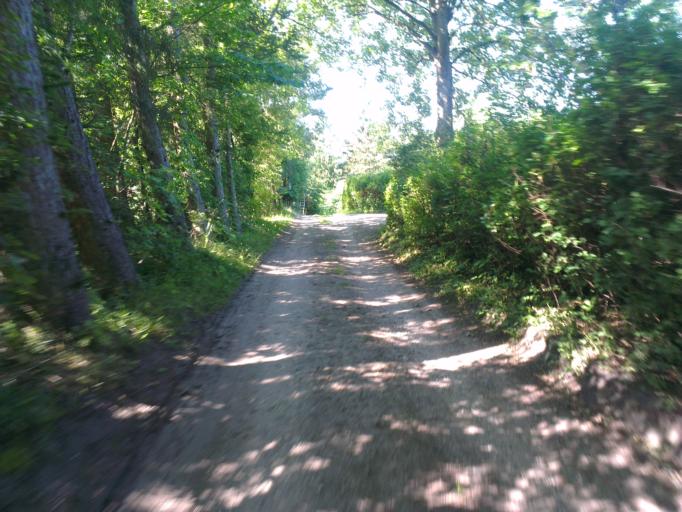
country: DK
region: Capital Region
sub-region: Frederikssund Kommune
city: Frederikssund
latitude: 55.7835
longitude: 12.0368
